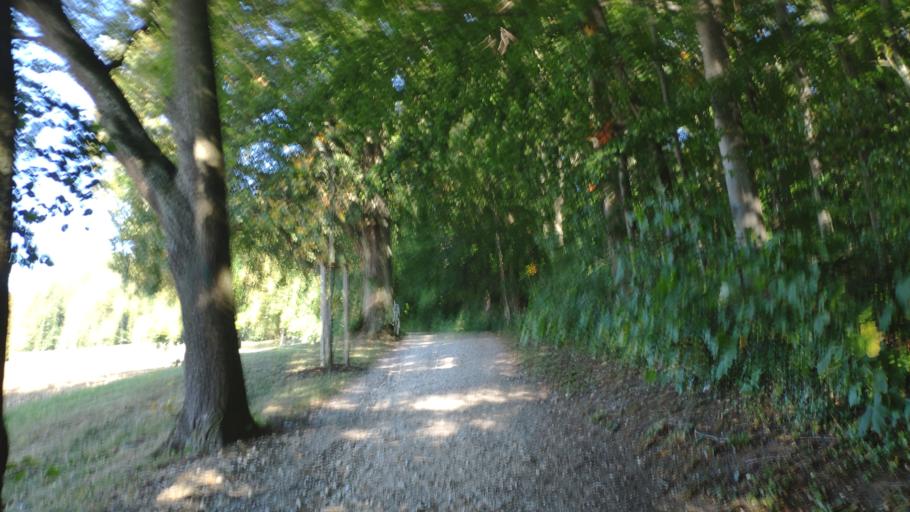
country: DE
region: Baden-Wuerttemberg
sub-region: Tuebingen Region
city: Ulm
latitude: 48.4163
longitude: 9.9567
